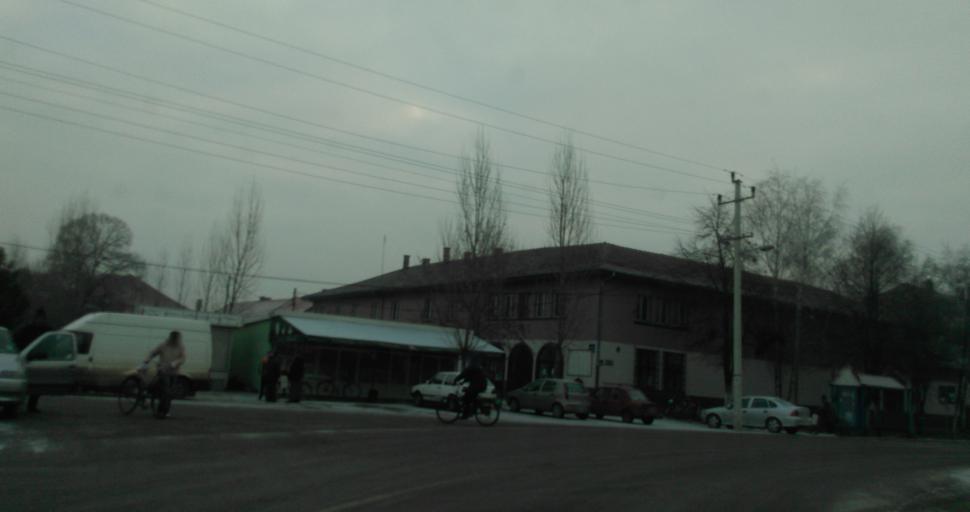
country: RS
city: Kumane
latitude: 45.5371
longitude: 20.2281
